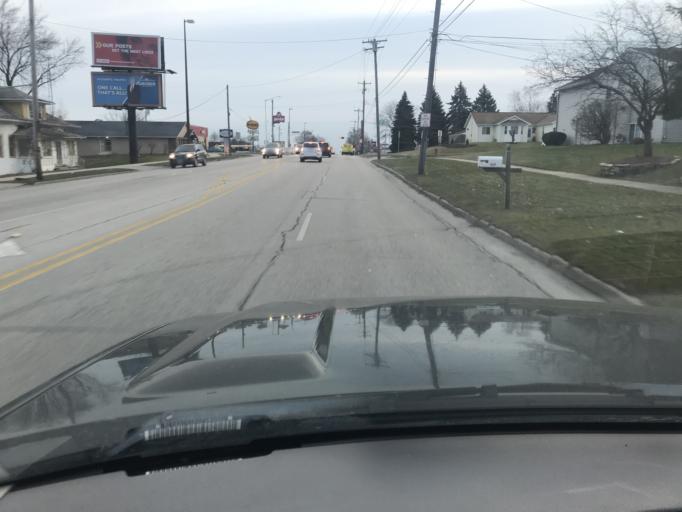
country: US
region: Wisconsin
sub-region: Kenosha County
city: Kenosha
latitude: 42.5885
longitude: -87.8653
